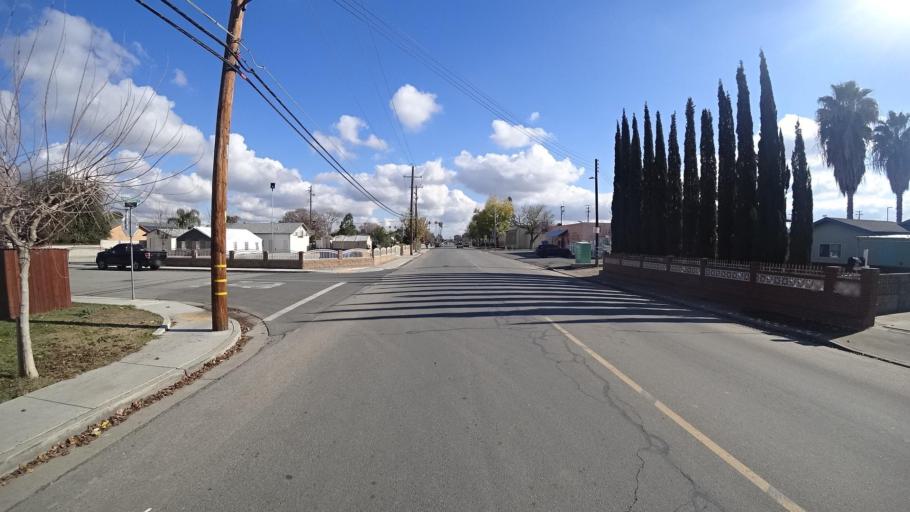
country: US
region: California
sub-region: Kern County
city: McFarland
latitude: 35.6744
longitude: -119.2330
